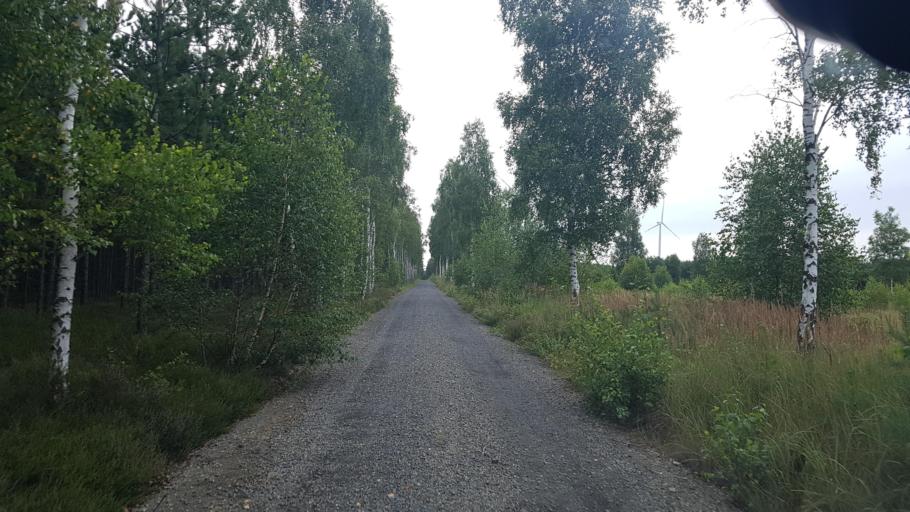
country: DE
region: Brandenburg
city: Grossraschen
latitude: 51.6245
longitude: 13.9786
